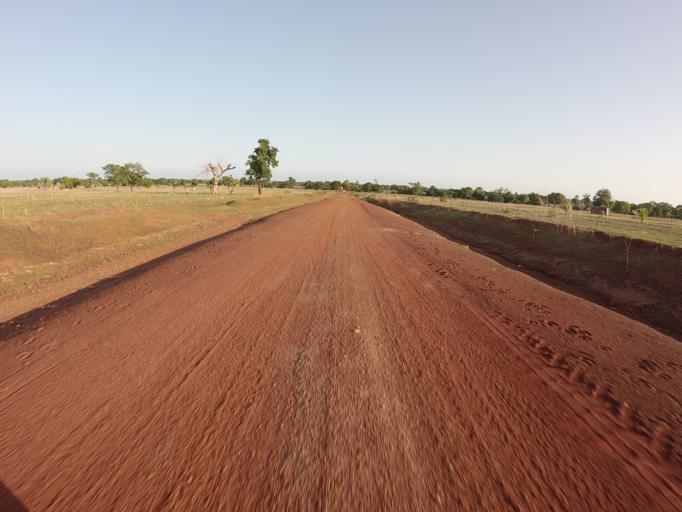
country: TG
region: Savanes
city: Sansanne-Mango
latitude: 10.3516
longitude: -0.0930
